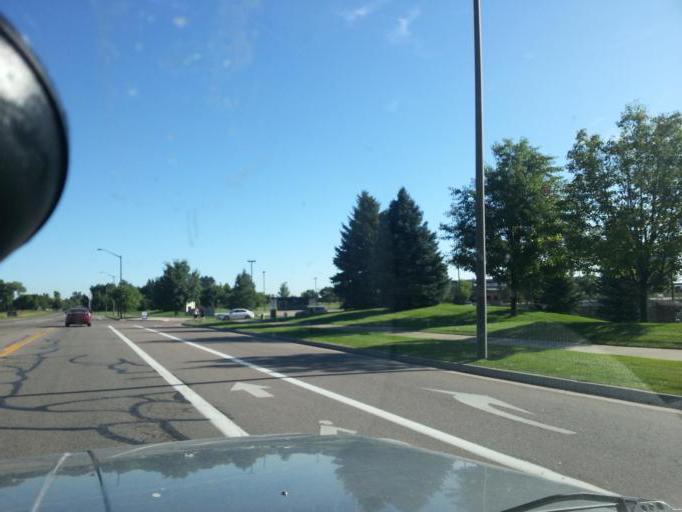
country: US
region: Colorado
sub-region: Larimer County
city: Fort Collins
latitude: 40.5023
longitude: -105.0392
